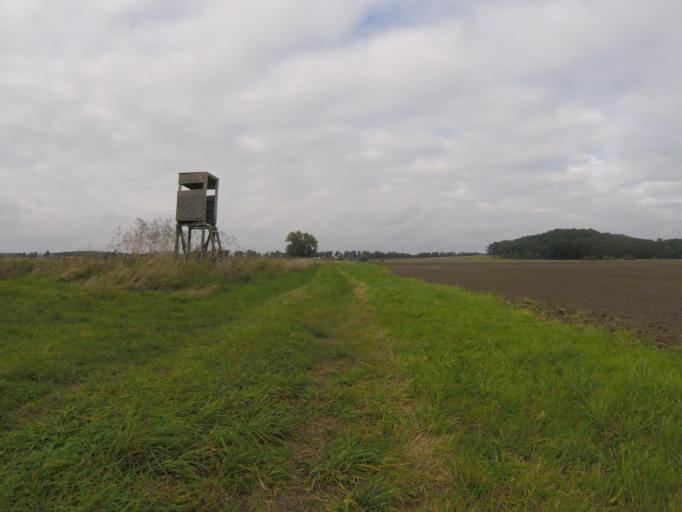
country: DE
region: Brandenburg
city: Mittenwalde
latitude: 52.2640
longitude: 13.4946
